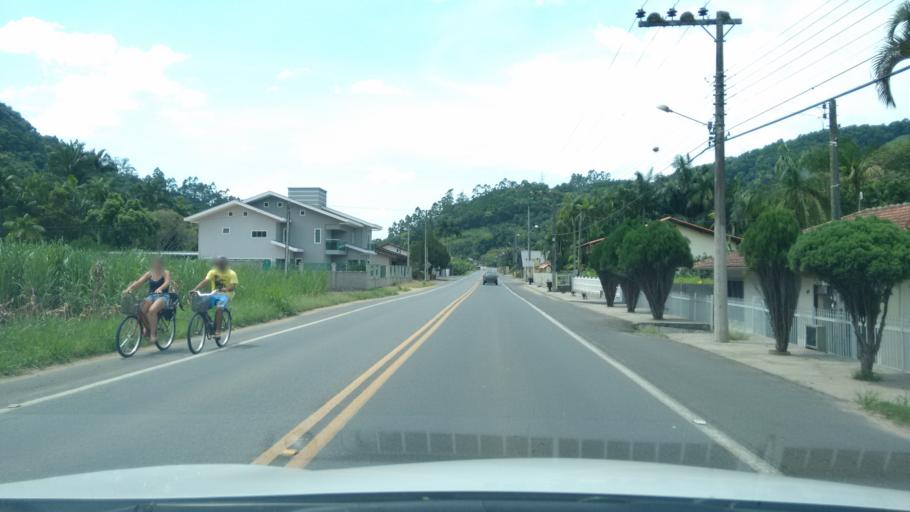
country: BR
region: Santa Catarina
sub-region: Rodeio
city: Gavea
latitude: -26.9011
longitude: -49.3572
